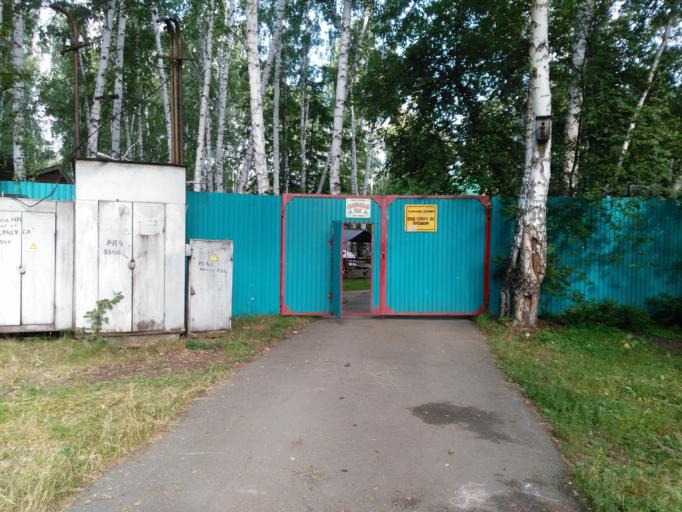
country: RU
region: Chelyabinsk
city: Tayginka
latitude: 55.4793
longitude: 60.4994
